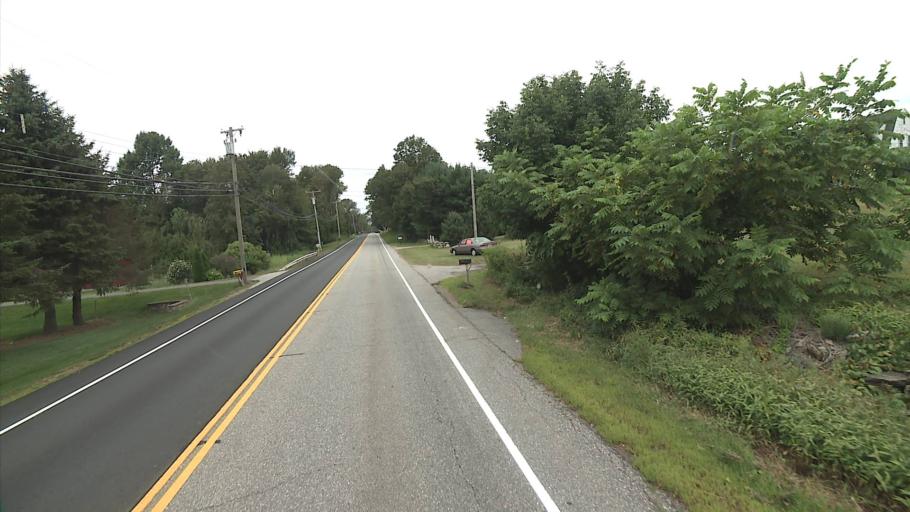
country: US
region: Connecticut
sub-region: Hartford County
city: Manchester
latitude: 41.7440
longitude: -72.4371
